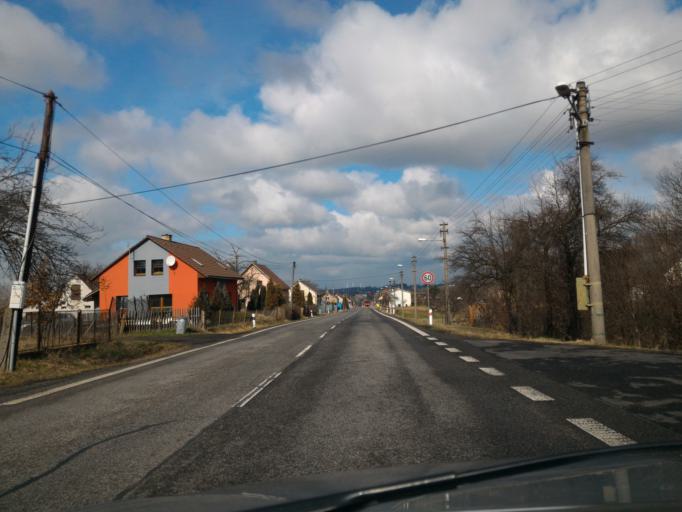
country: PL
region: Silesian Voivodeship
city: Zawidow
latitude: 51.0138
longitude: 15.0671
